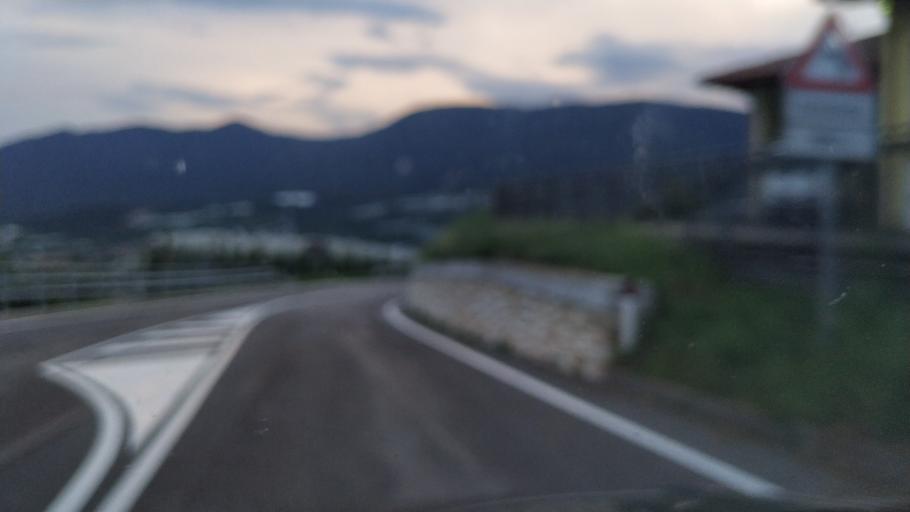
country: IT
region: Trentino-Alto Adige
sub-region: Provincia di Trento
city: Fondo
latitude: 46.4414
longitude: 11.1301
